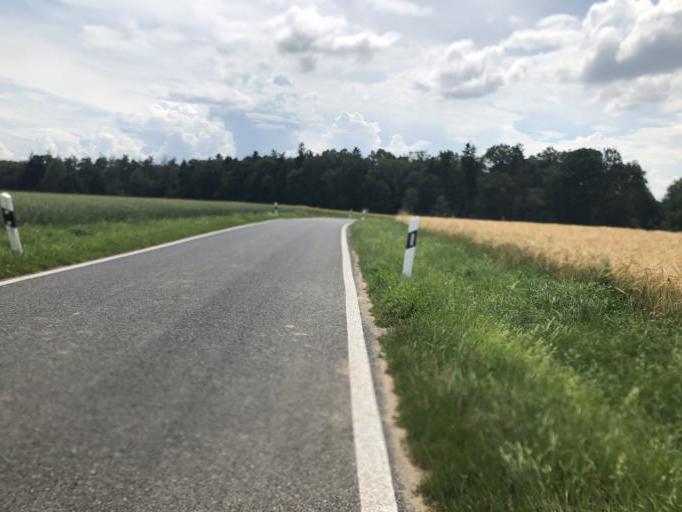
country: DE
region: Bavaria
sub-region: Regierungsbezirk Mittelfranken
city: Herzogenaurach
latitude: 49.5755
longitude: 10.9373
